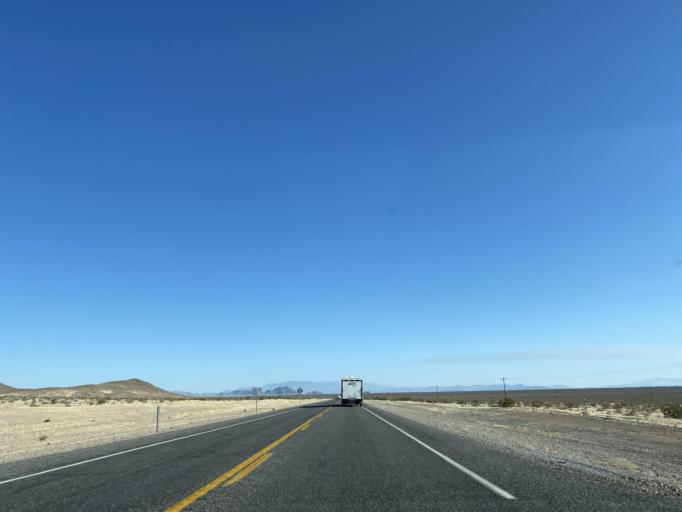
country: US
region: Nevada
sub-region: Nye County
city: Beatty
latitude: 36.6804
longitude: -116.5422
